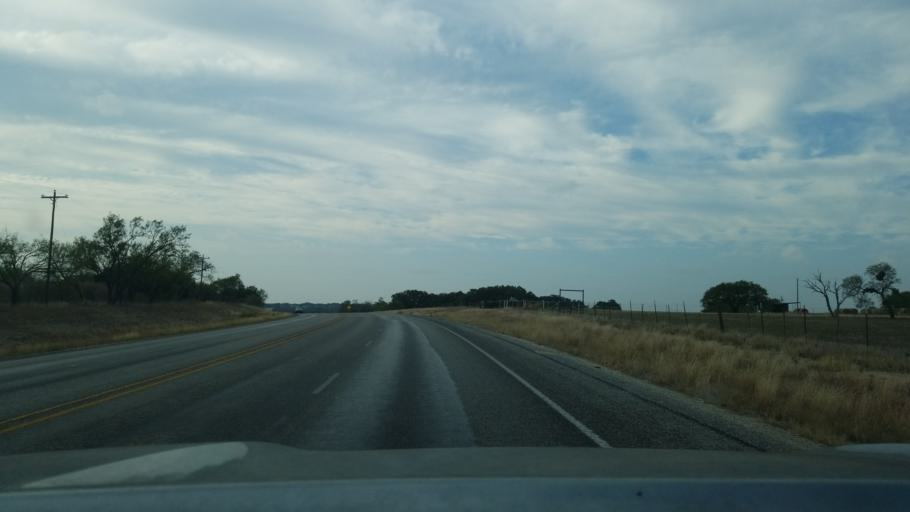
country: US
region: Texas
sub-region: Mills County
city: Goldthwaite
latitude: 31.5462
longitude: -98.6333
